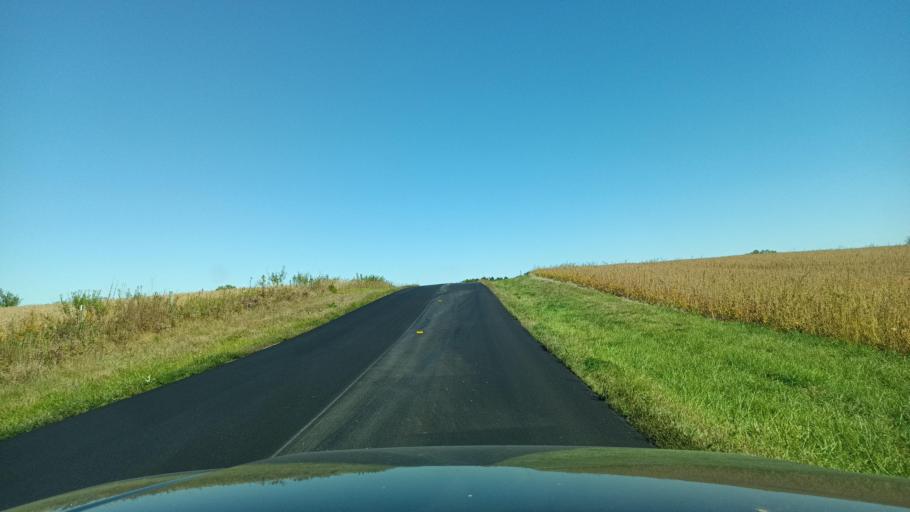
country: US
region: Missouri
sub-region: Macon County
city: La Plata
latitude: 39.9273
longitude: -92.5448
